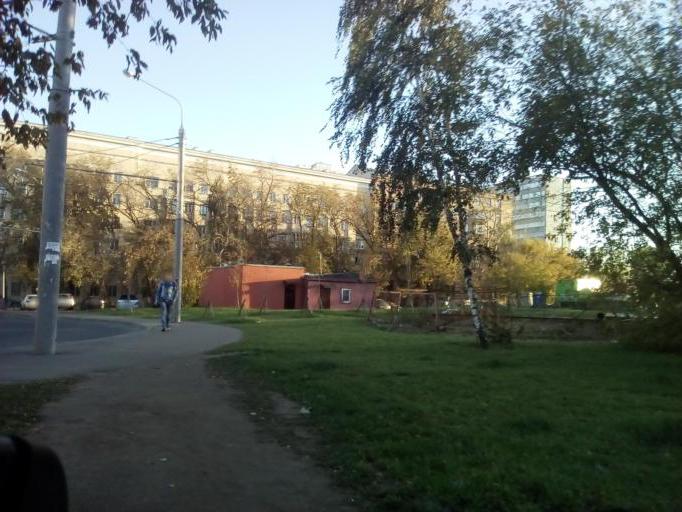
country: RU
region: Moskovskaya
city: Koptevo
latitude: 55.8243
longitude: 37.4931
